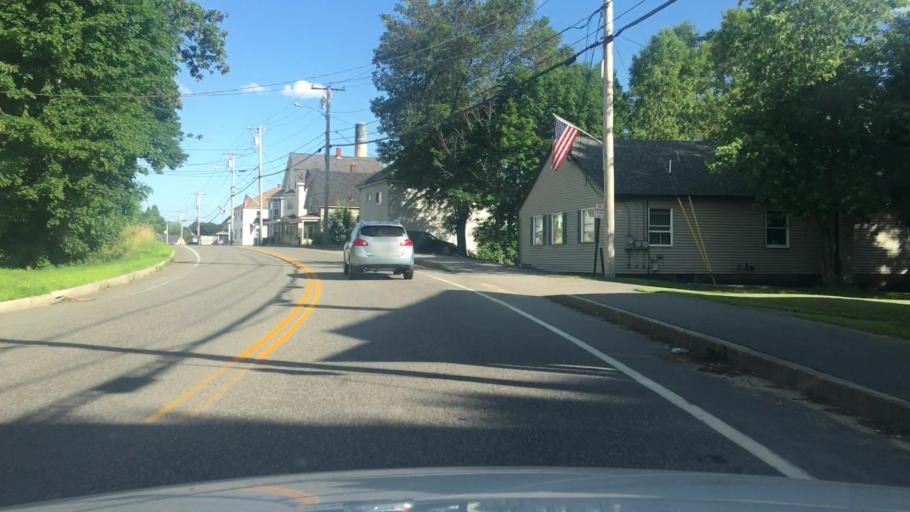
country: US
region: Maine
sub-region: Franklin County
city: Chisholm
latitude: 44.4819
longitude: -70.2000
